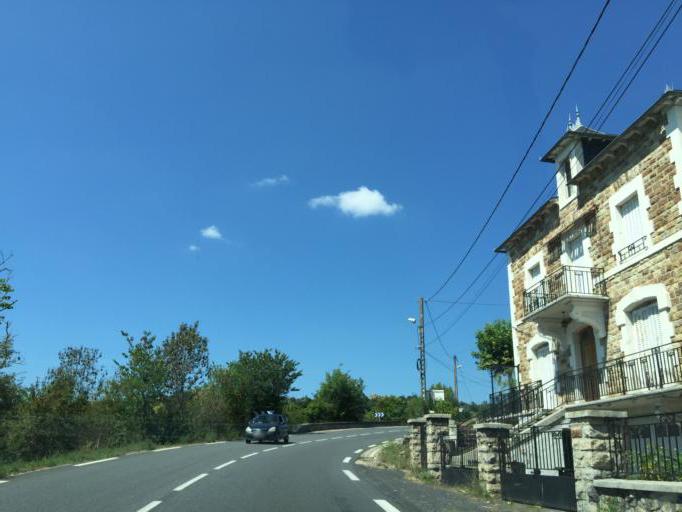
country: FR
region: Midi-Pyrenees
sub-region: Departement de l'Aveyron
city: Espalion
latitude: 44.5291
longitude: 2.7623
